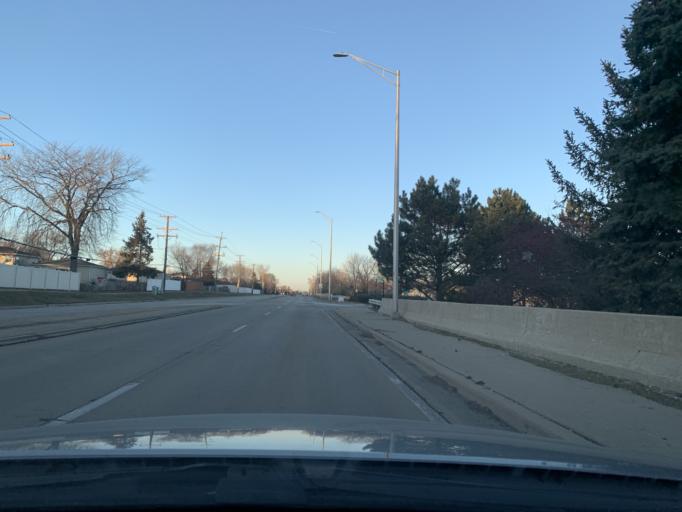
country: US
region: Illinois
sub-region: Cook County
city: Schaumburg
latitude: 42.0178
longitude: -88.0603
